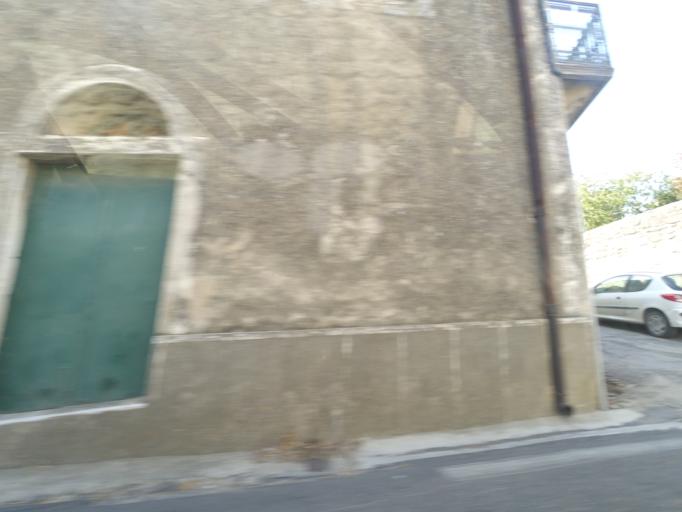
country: FR
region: Languedoc-Roussillon
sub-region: Departement du Gard
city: Villevieille
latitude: 43.8134
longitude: 4.1218
